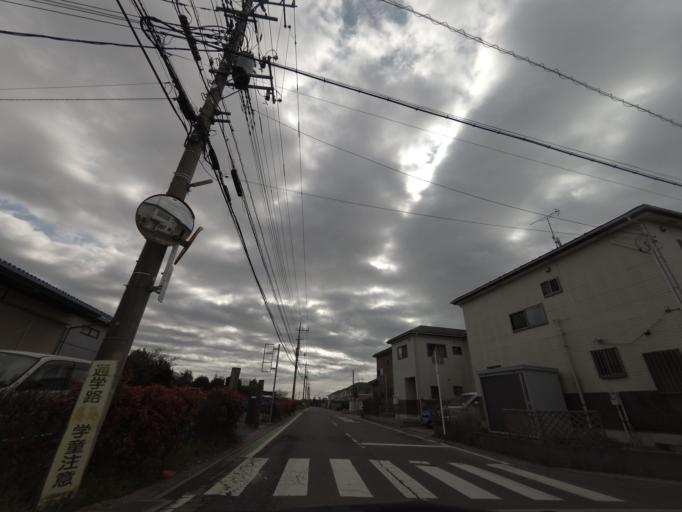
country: JP
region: Saitama
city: Kamifukuoka
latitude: 35.8917
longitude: 139.5426
